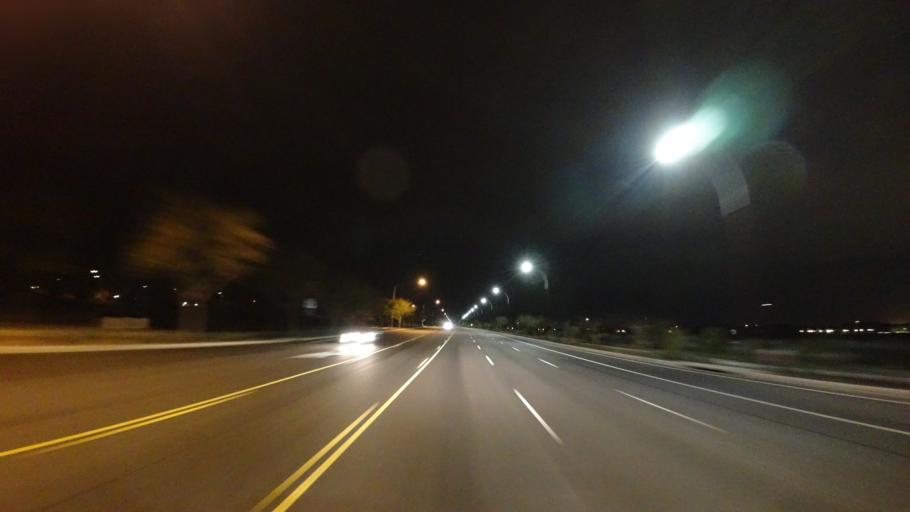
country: US
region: Arizona
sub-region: Maricopa County
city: Queen Creek
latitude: 33.3340
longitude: -111.6009
